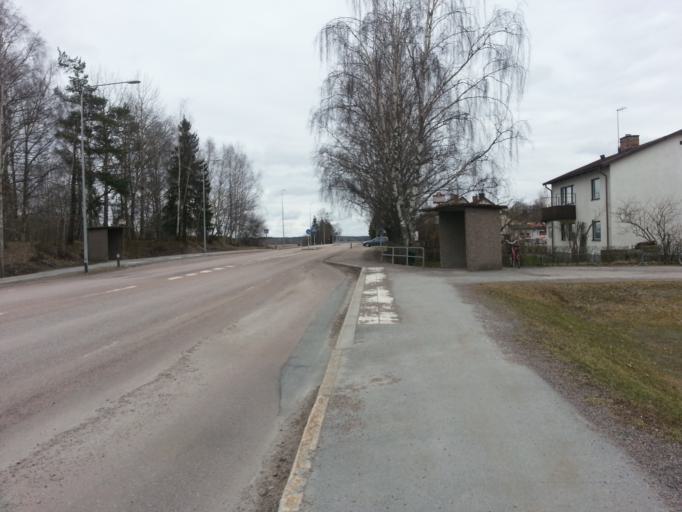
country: SE
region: Uppsala
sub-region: Osthammars Kommun
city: Gimo
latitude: 60.1682
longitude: 18.1935
